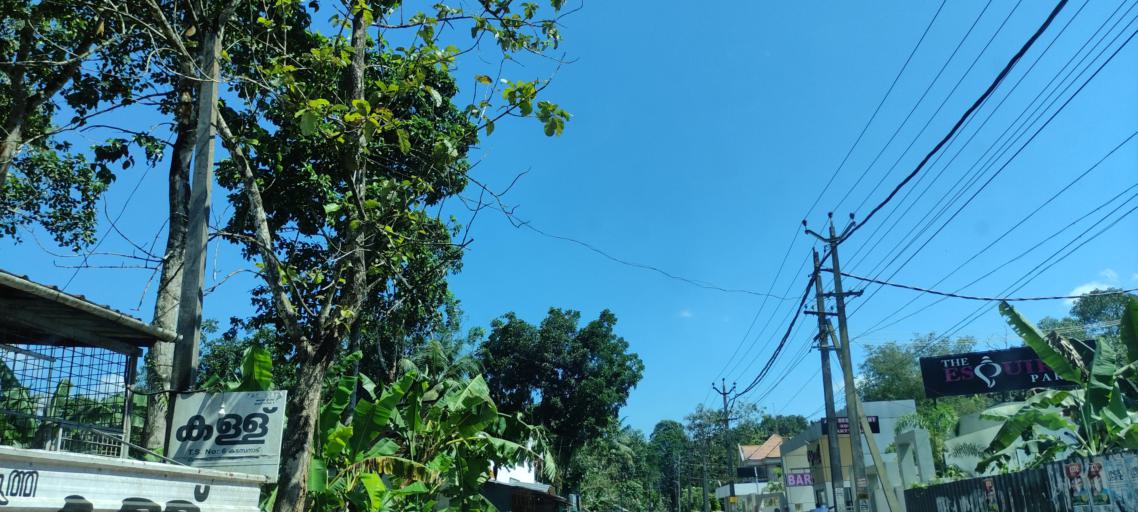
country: IN
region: Kerala
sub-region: Pattanamtitta
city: Adur
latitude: 9.0906
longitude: 76.6908
